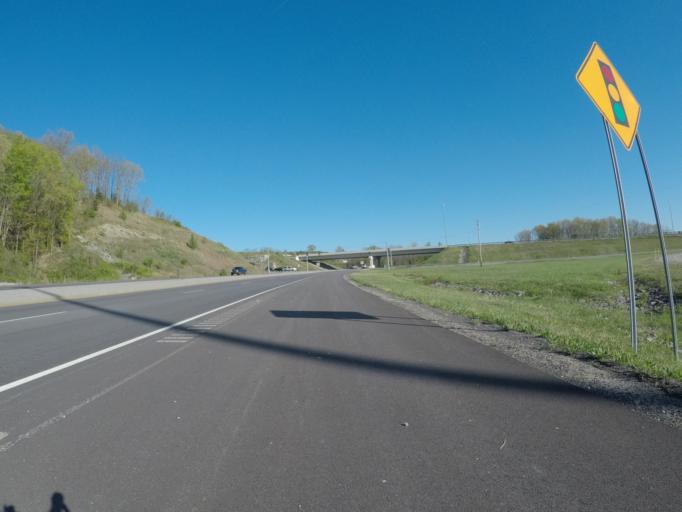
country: US
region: Kentucky
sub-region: Boyd County
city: Meads
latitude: 38.3706
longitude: -82.7005
